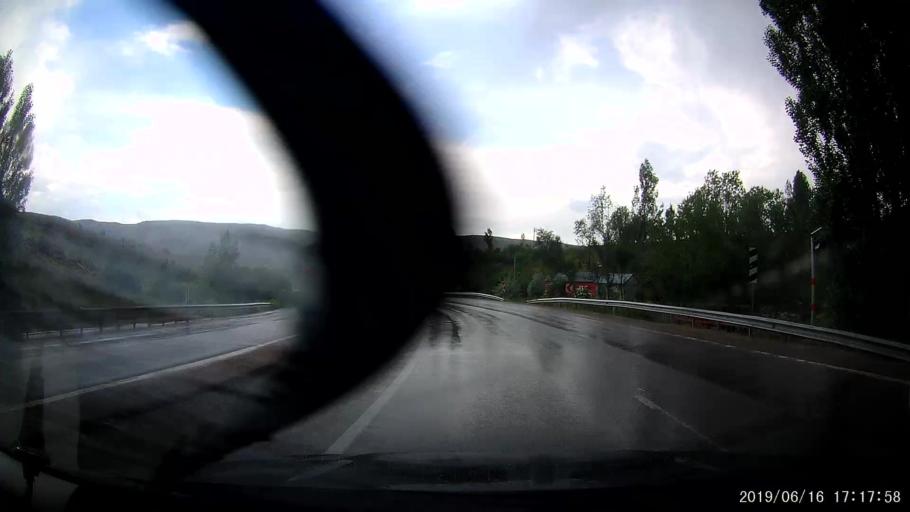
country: TR
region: Erzincan
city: Tercan
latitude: 39.8205
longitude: 40.5291
